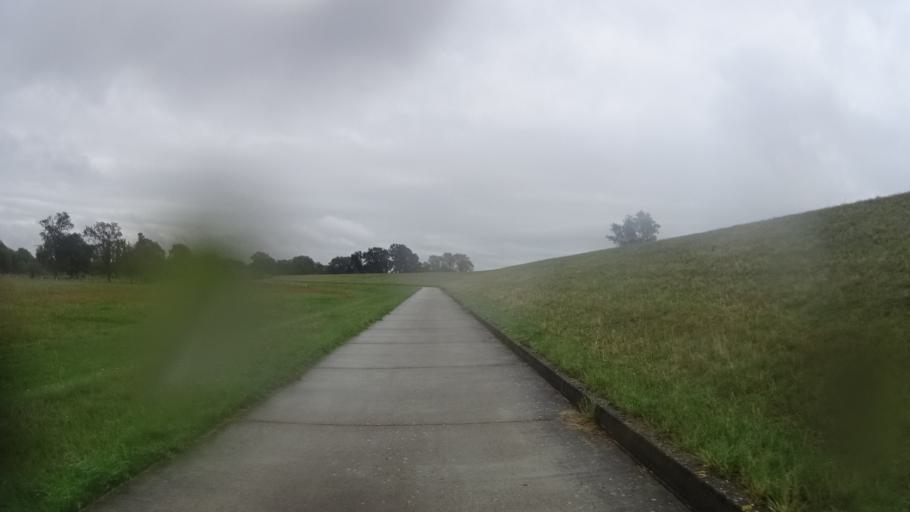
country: DE
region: Lower Saxony
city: Damnatz
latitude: 53.1735
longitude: 11.1604
